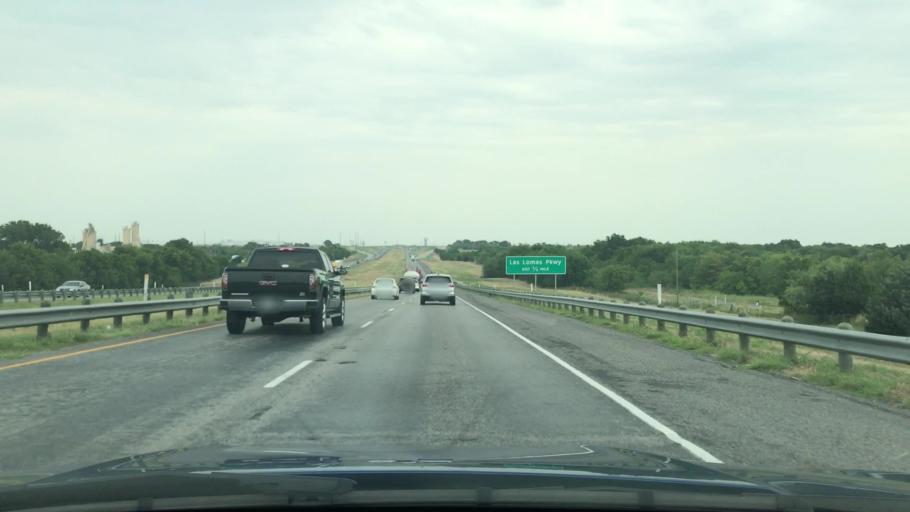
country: US
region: Texas
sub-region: Kaufman County
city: Talty
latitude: 32.7370
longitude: -96.3539
